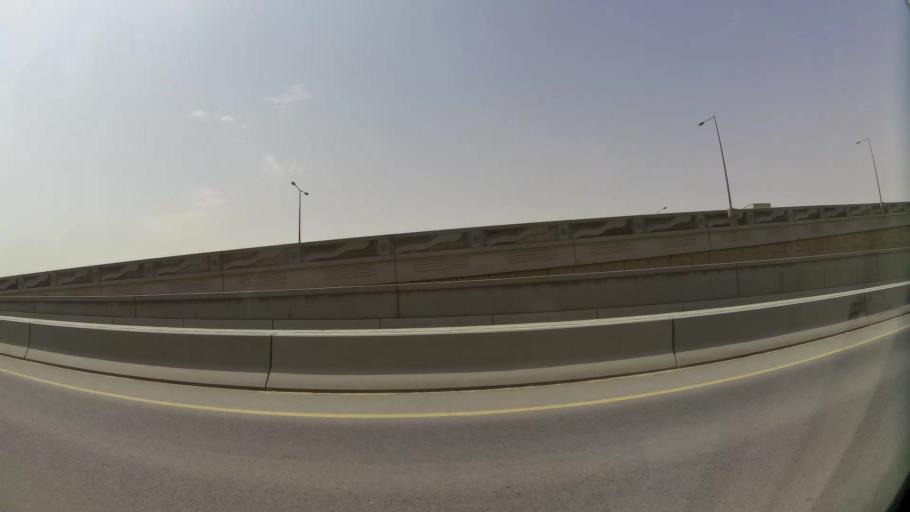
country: QA
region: Baladiyat ar Rayyan
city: Ar Rayyan
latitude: 25.2235
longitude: 51.4334
